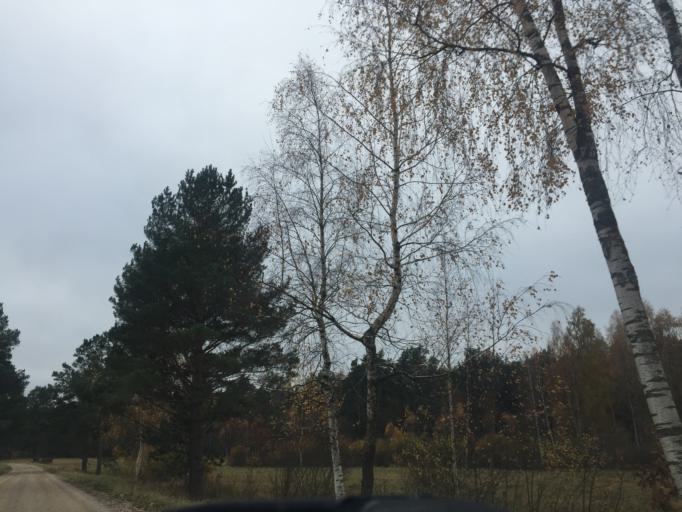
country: LV
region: Jaunpils
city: Jaunpils
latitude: 56.6947
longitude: 23.1165
